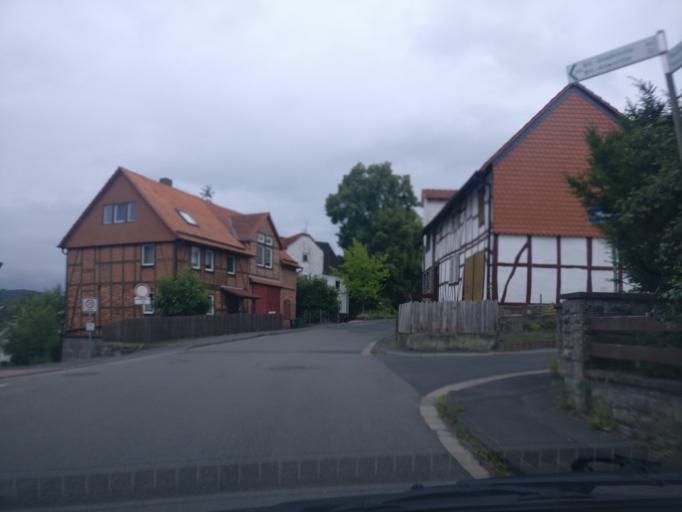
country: DE
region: Hesse
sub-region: Regierungsbezirk Kassel
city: Baunatal
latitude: 51.2756
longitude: 9.3691
